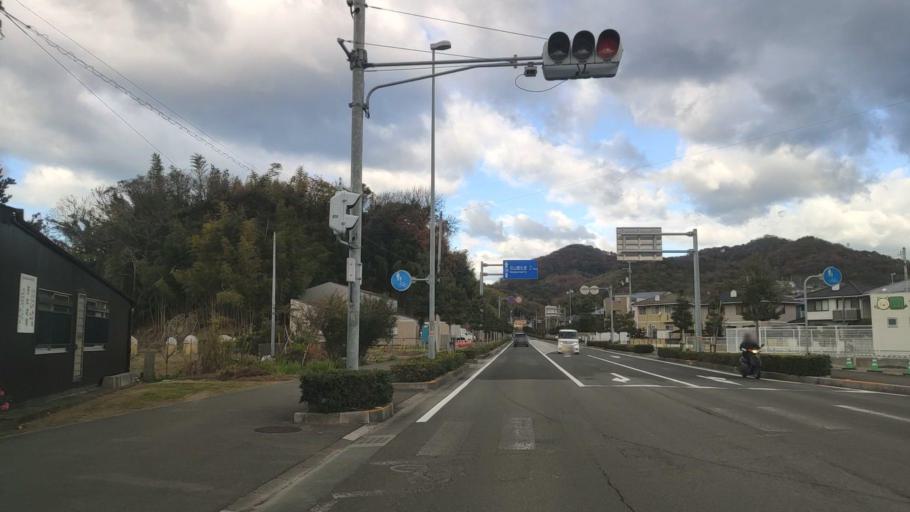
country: JP
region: Ehime
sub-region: Shikoku-chuo Shi
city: Matsuyama
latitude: 33.8720
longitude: 132.7195
